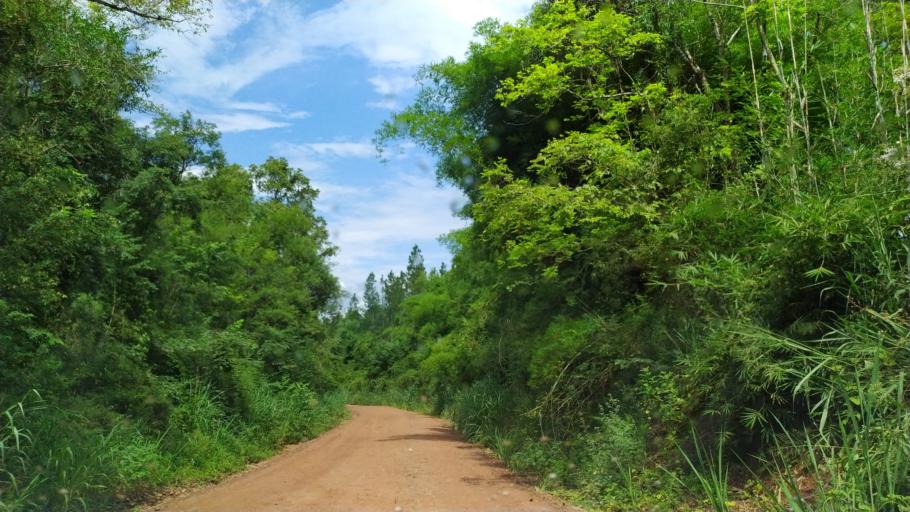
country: AR
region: Misiones
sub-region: Departamento de Eldorado
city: Eldorado
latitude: -26.4807
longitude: -54.5924
